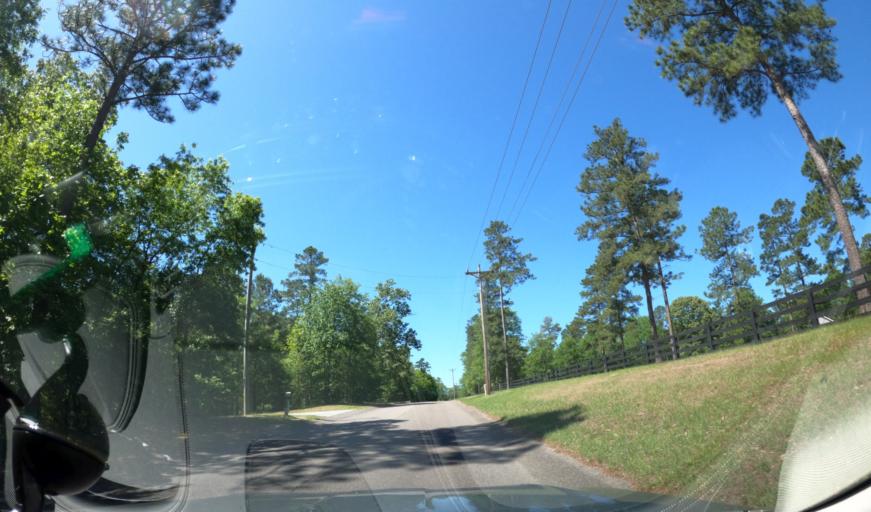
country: US
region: South Carolina
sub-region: Aiken County
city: Langley
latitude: 33.4490
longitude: -81.8010
